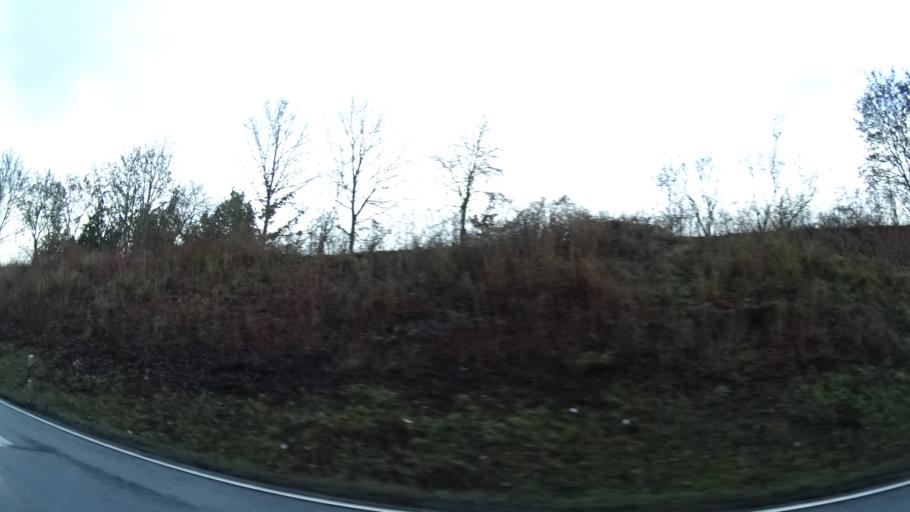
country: DE
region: Hesse
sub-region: Regierungsbezirk Giessen
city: Lich
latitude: 50.5503
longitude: 8.7711
